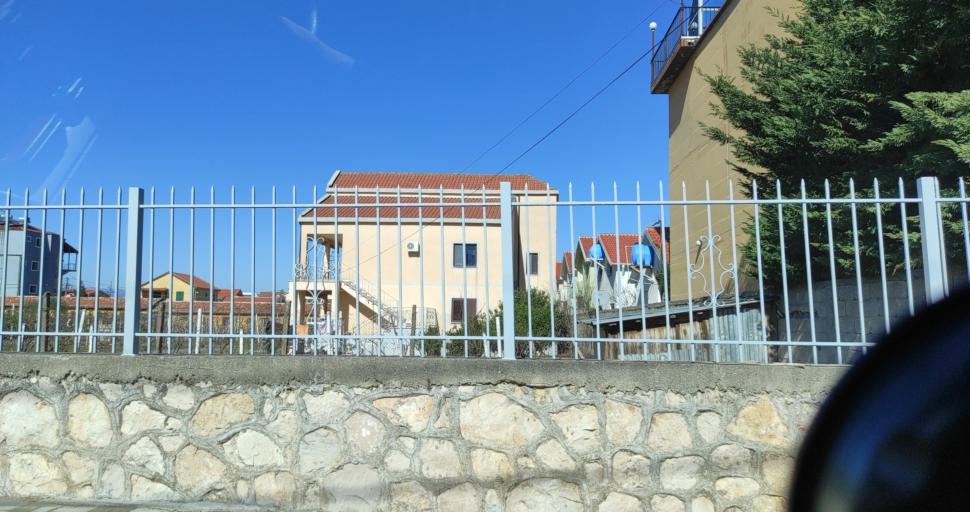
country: AL
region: Shkoder
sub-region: Rrethi i Shkodres
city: Velipoje
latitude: 41.8624
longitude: 19.4390
